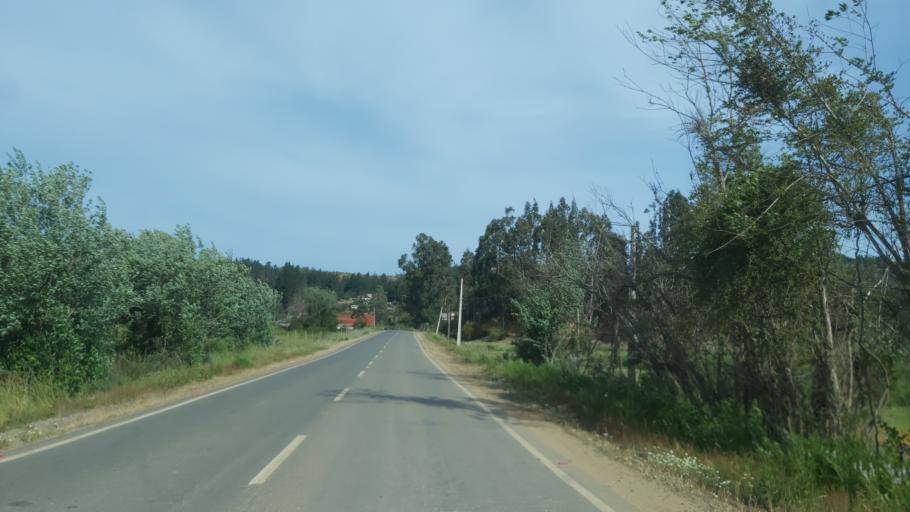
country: CL
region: Maule
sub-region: Provincia de Talca
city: Constitucion
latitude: -34.8497
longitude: -72.0447
